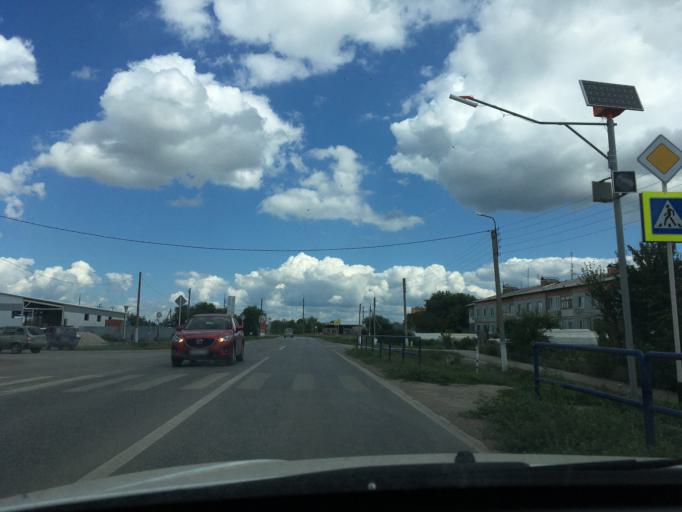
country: RU
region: Samara
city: Bezenchuk
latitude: 52.9942
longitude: 49.4379
